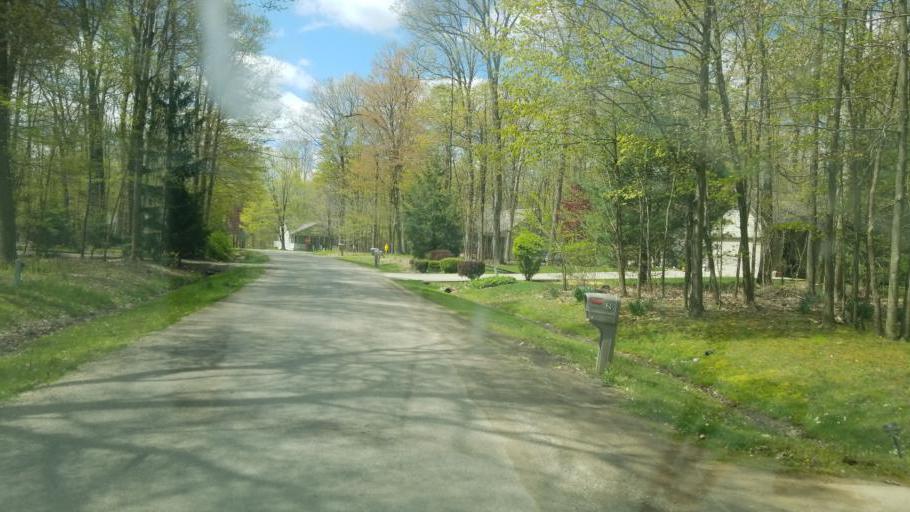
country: US
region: Ohio
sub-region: Knox County
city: Gambier
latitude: 40.4441
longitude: -82.3502
